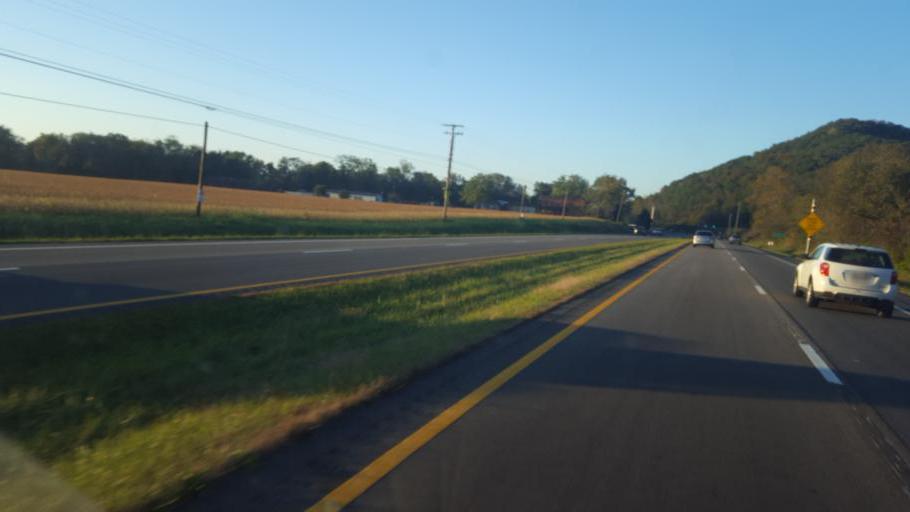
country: US
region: Ohio
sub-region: Scioto County
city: Lucasville
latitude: 38.8381
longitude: -82.9842
